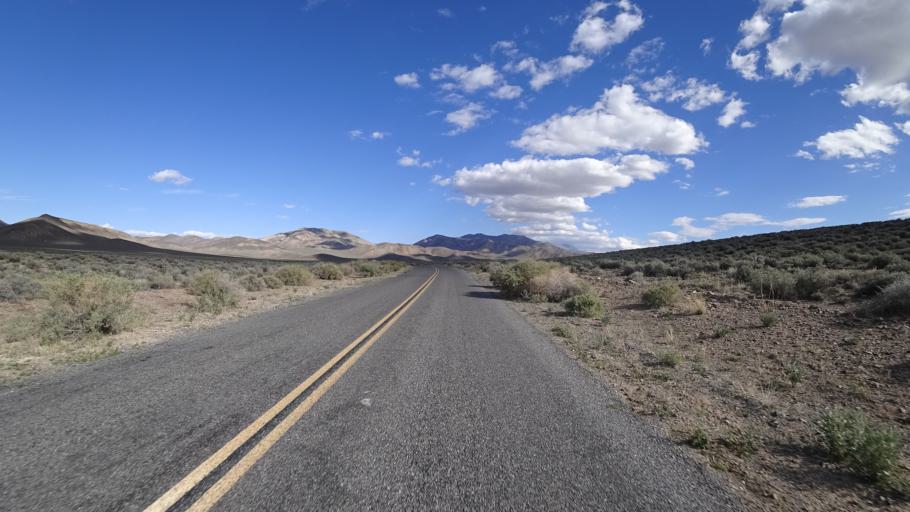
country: US
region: Nevada
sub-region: Nye County
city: Beatty
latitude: 36.3832
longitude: -117.1492
